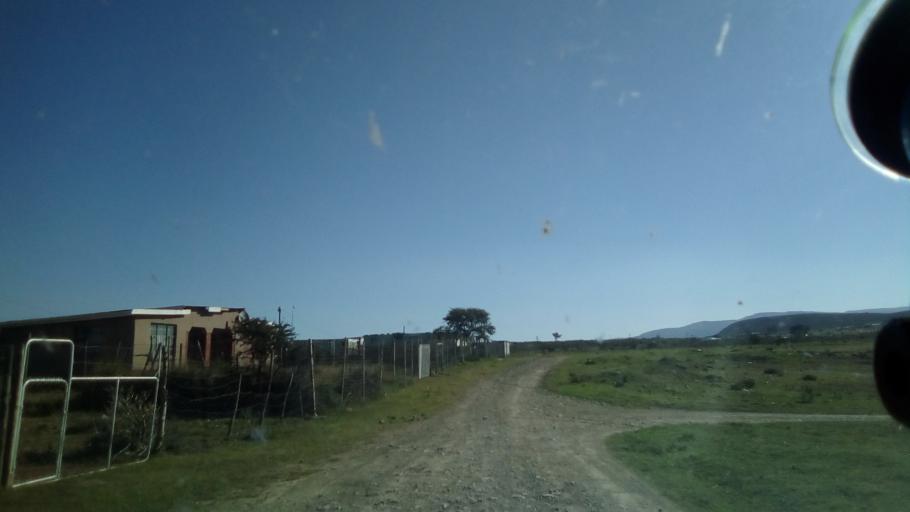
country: ZA
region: Eastern Cape
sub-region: Buffalo City Metropolitan Municipality
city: Bhisho
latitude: -32.8299
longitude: 27.3686
